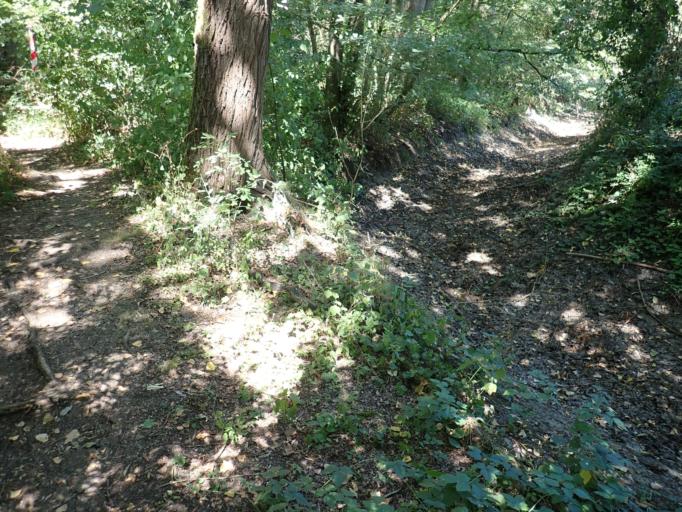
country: BE
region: Flanders
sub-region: Provincie Vlaams-Brabant
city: Haacht
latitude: 50.9669
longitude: 4.6552
